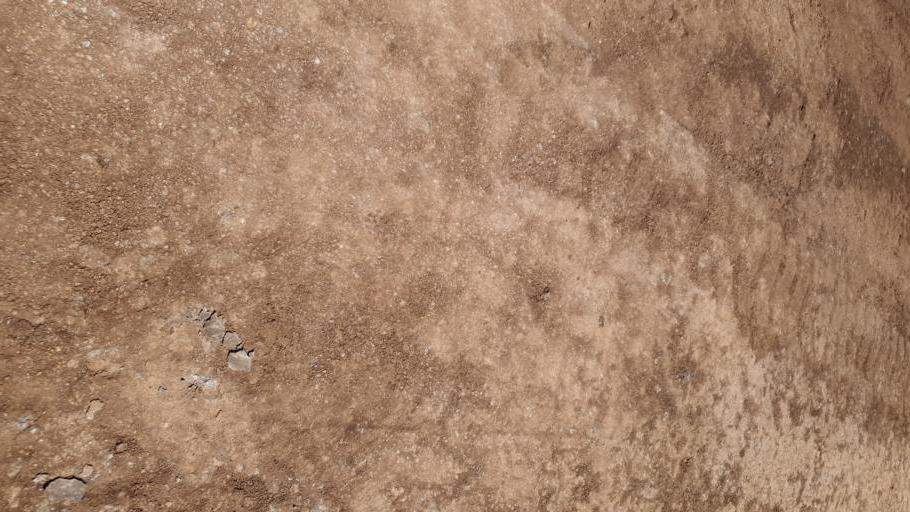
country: ET
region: Oromiya
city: Fiche
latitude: 9.6367
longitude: 38.9639
